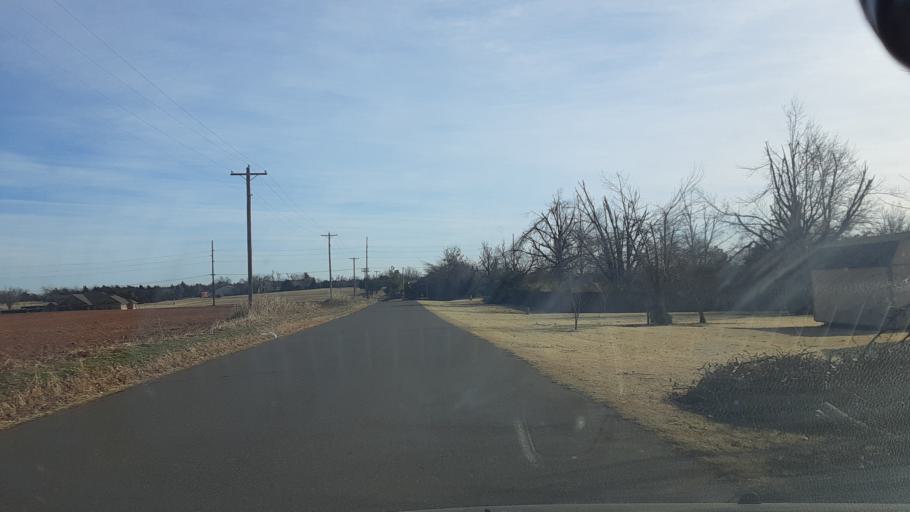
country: US
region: Oklahoma
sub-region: Logan County
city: Guthrie
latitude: 35.8924
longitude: -97.4102
